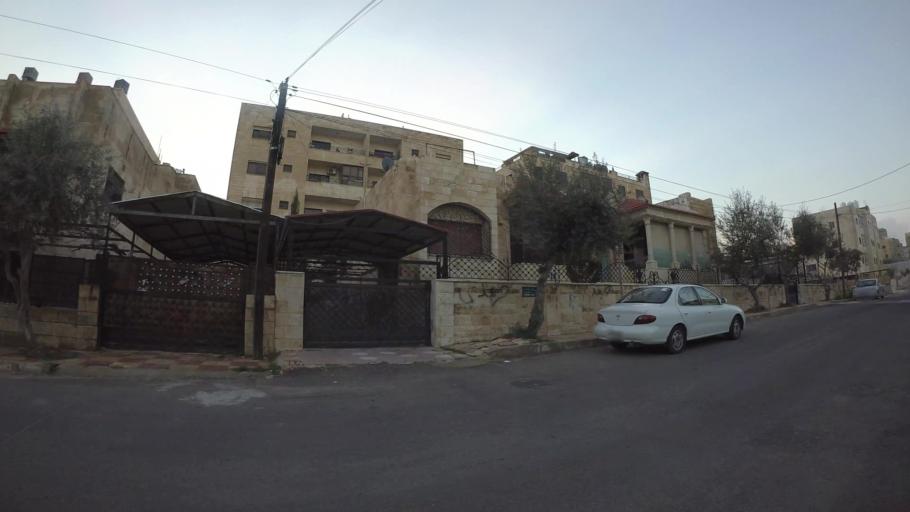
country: JO
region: Amman
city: Amman
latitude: 31.9964
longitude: 35.9482
